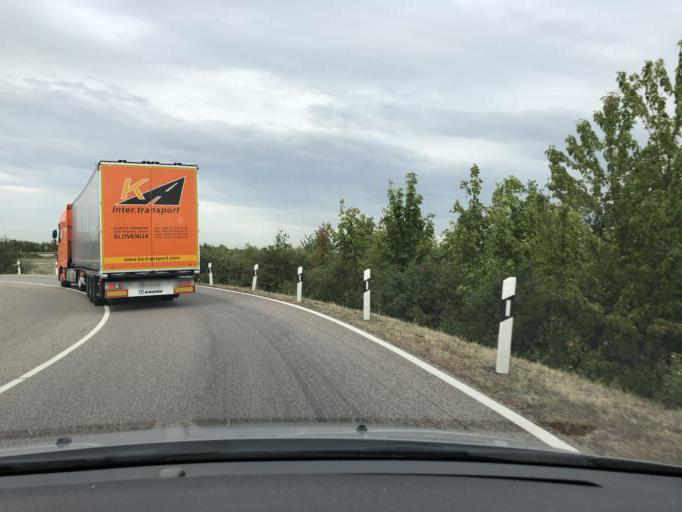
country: DE
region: Saxony-Anhalt
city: Brehna
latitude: 51.5693
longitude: 12.2213
